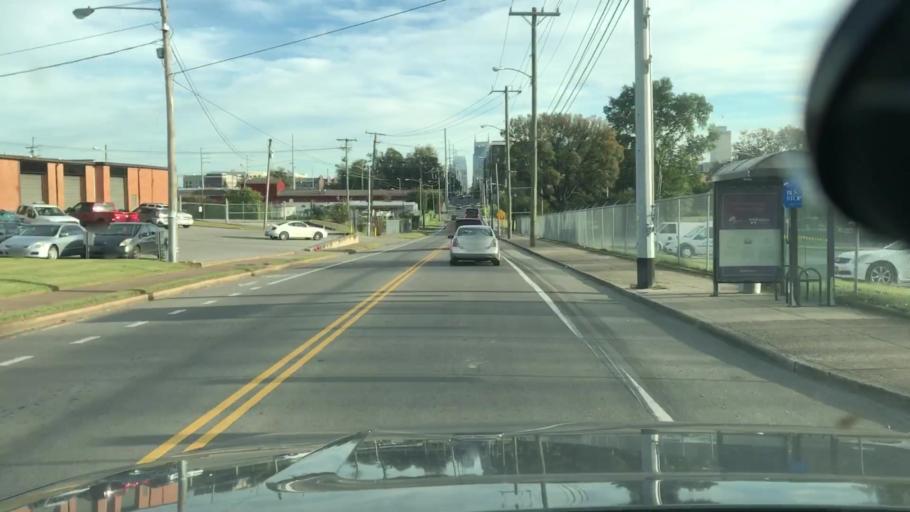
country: US
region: Tennessee
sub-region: Davidson County
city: Nashville
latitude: 36.1832
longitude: -86.7900
